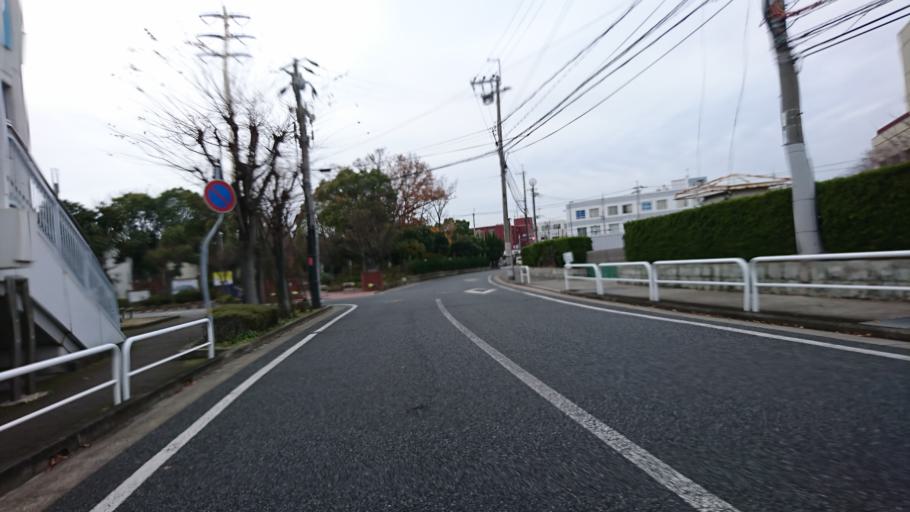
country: JP
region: Hyogo
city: Kakogawacho-honmachi
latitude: 34.7564
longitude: 134.8398
